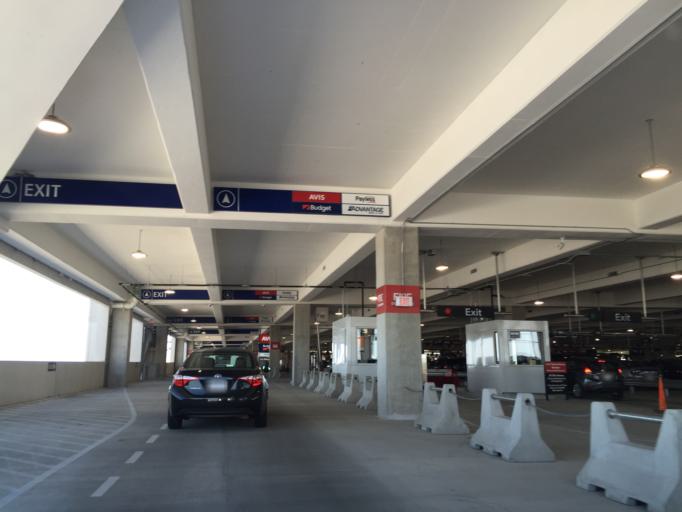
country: US
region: Texas
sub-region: Travis County
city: Hornsby Bend
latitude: 30.2053
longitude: -97.6668
